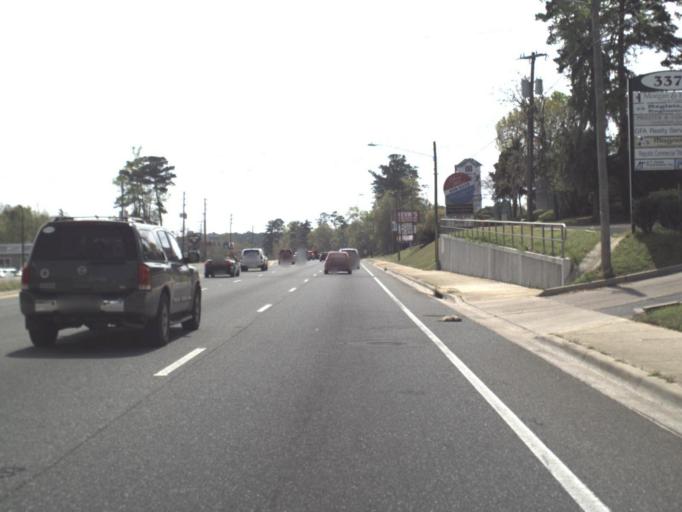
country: US
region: Florida
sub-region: Leon County
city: Tallahassee
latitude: 30.4988
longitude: -84.2472
